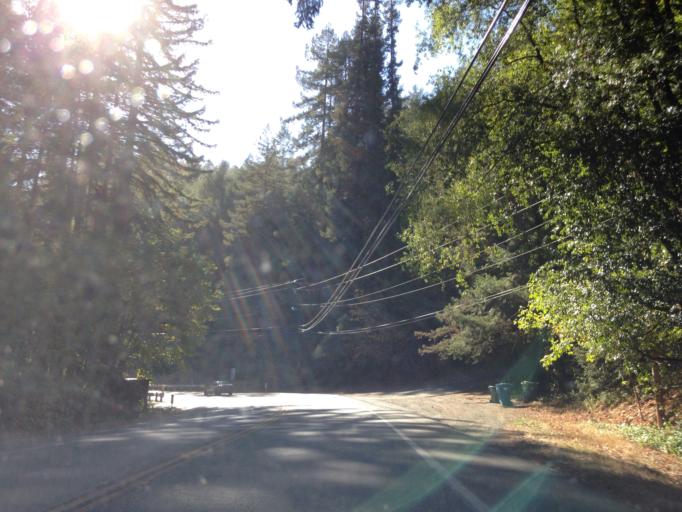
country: US
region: California
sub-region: Sonoma County
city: Monte Rio
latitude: 38.4743
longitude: -123.0046
